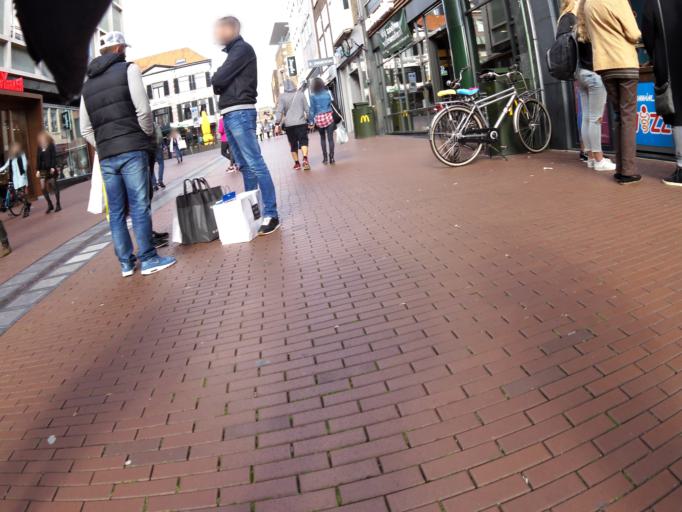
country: NL
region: Gelderland
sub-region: Gemeente Nijmegen
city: Nijmegen
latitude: 51.8468
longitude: 5.8647
